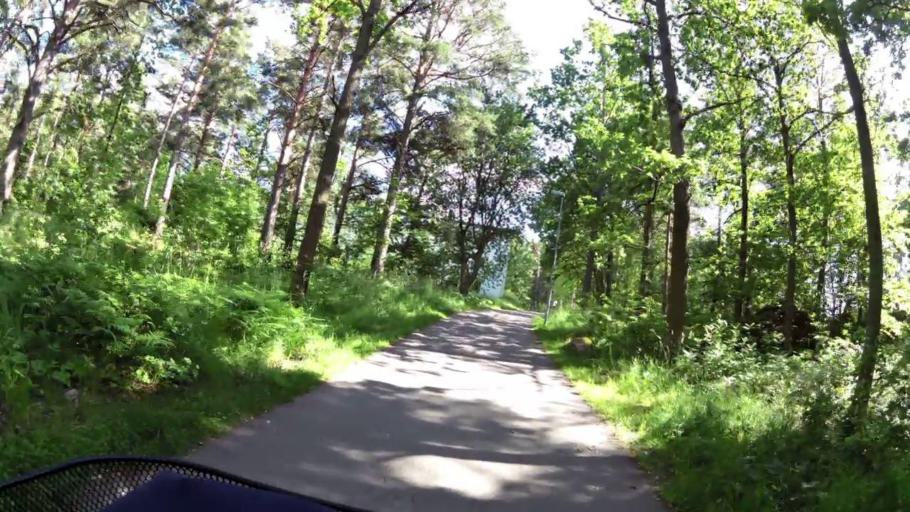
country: SE
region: OEstergoetland
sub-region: Linkopings Kommun
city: Linkoping
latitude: 58.3949
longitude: 15.6579
